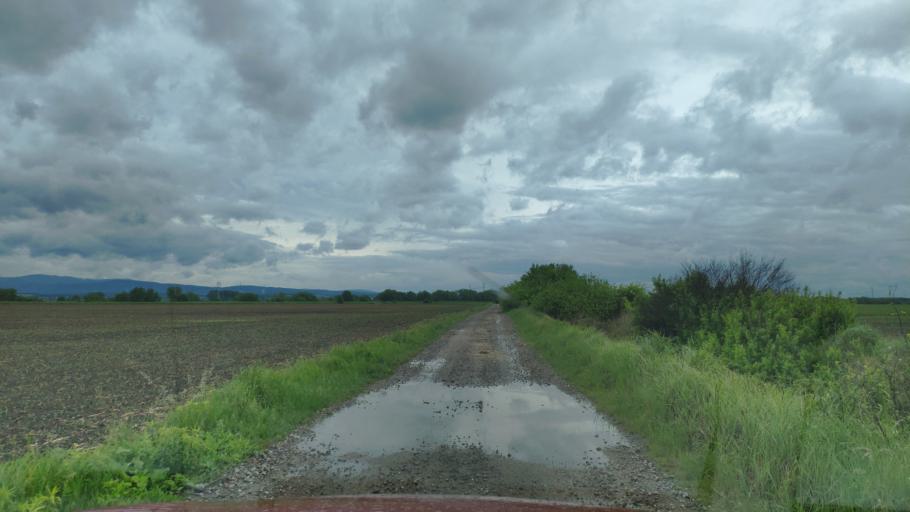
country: SK
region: Kosicky
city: Moldava nad Bodvou
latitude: 48.5524
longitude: 21.1146
